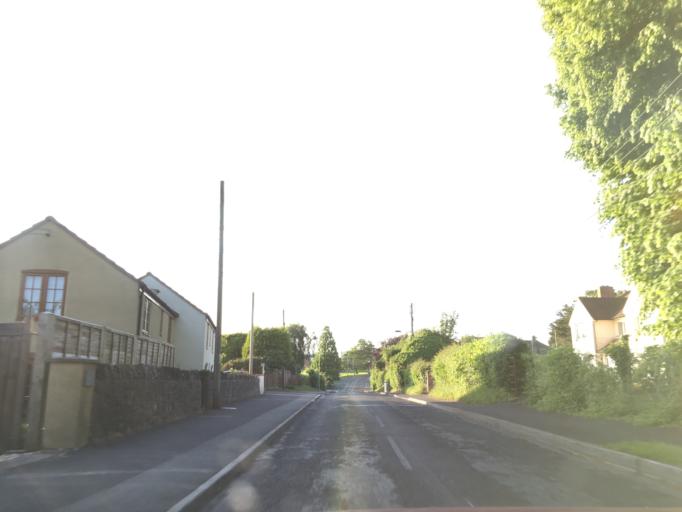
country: GB
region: England
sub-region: South Gloucestershire
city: Alveston
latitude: 51.5873
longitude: -2.5312
